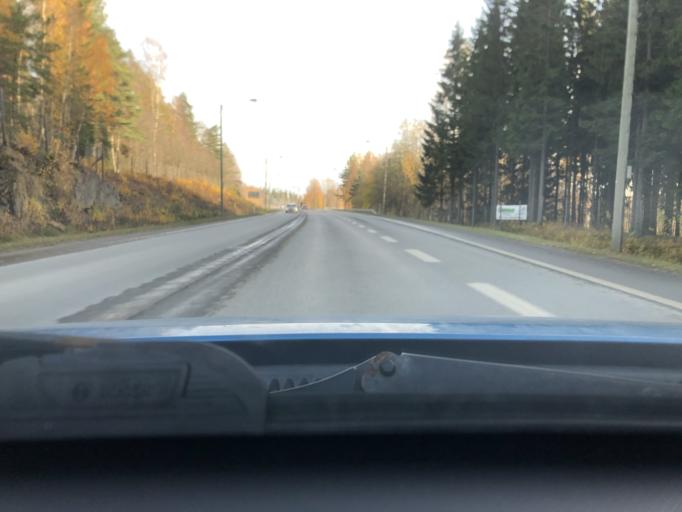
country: FI
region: Pirkanmaa
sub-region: Tampere
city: Kangasala
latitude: 61.4848
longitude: 23.9609
